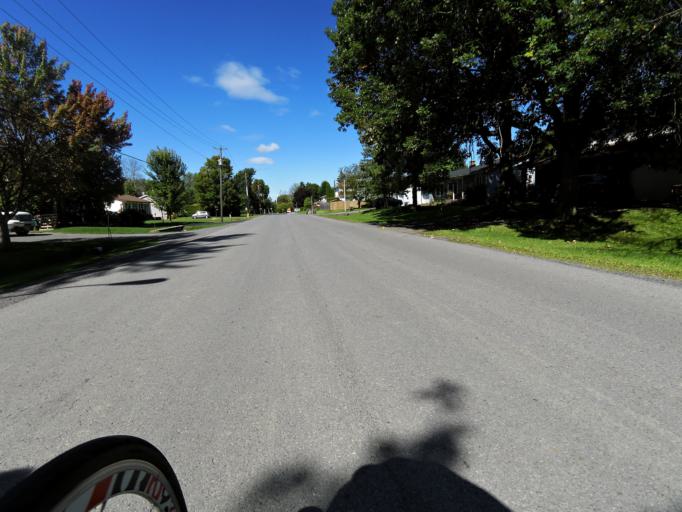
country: CA
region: Ontario
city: Bells Corners
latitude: 45.1903
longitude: -75.8262
